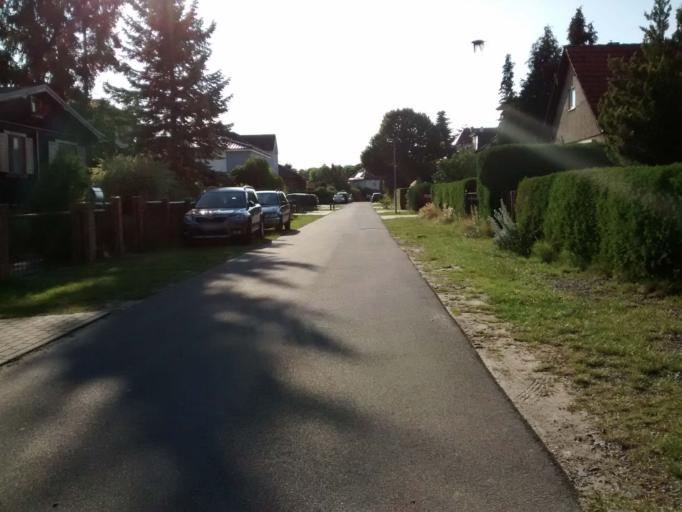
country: DE
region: Brandenburg
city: Hohen Neuendorf
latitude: 52.6608
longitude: 13.2798
